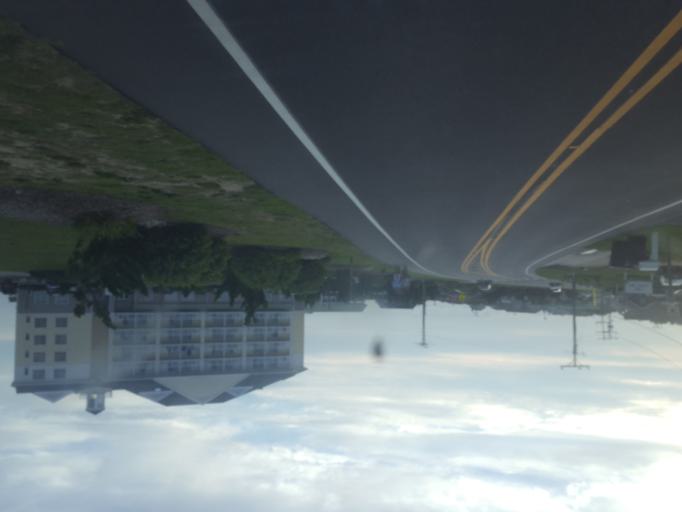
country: US
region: North Carolina
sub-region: Dare County
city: Kitty Hawk
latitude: 36.0994
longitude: -75.7110
